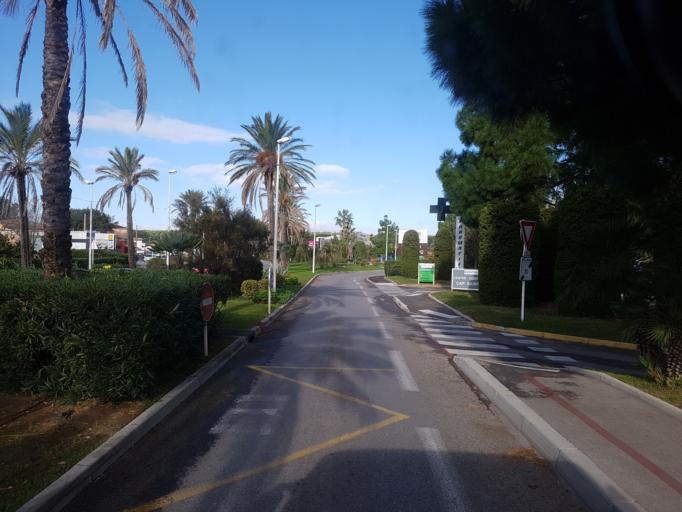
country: FR
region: Provence-Alpes-Cote d'Azur
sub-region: Departement du Var
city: Saint-Cyr-sur-Mer
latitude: 43.1823
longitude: 5.6955
